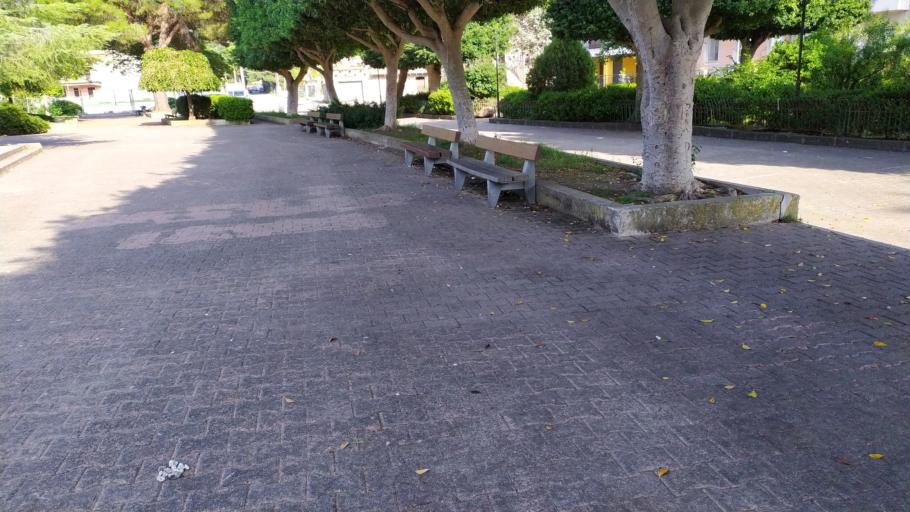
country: IT
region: Sicily
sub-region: Messina
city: Gualtieri Sicamino
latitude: 38.1646
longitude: 15.3194
